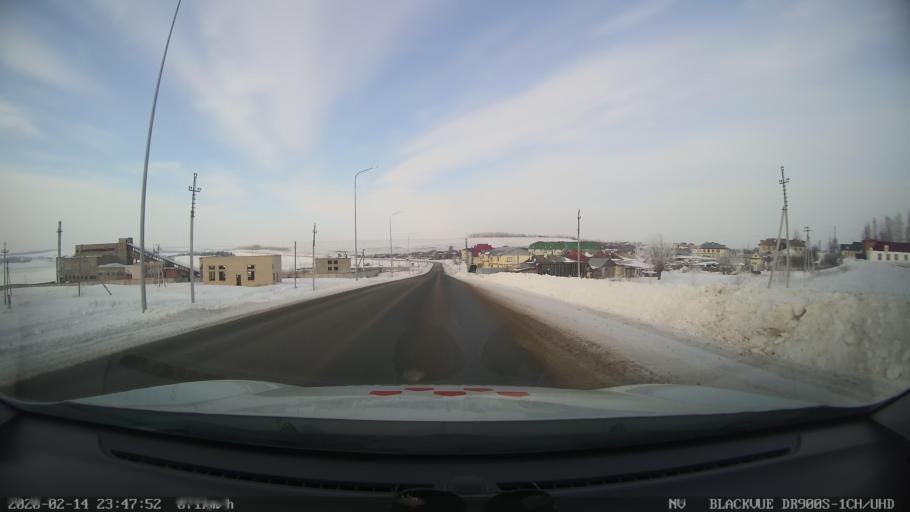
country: RU
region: Tatarstan
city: Kuybyshevskiy Zaton
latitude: 55.2437
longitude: 49.2066
